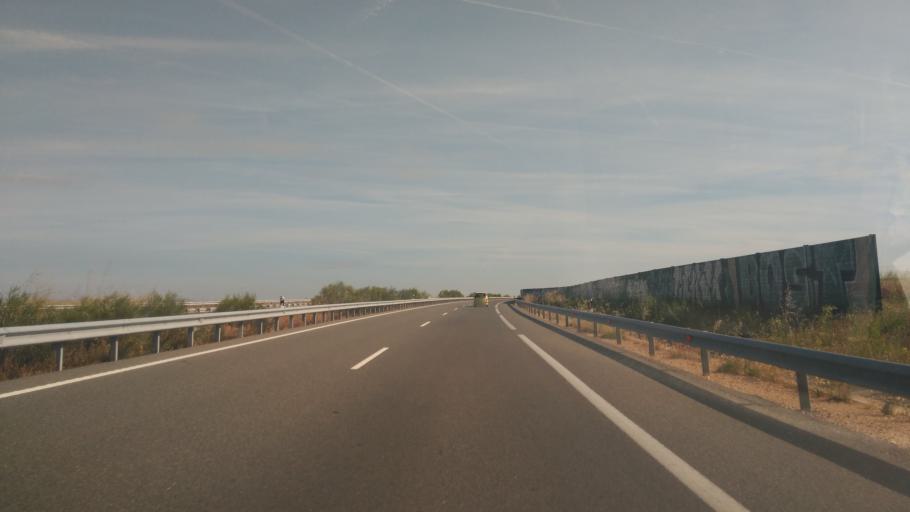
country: ES
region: Castille and Leon
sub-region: Provincia de Salamanca
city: Villamayor
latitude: 41.0165
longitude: -5.6797
